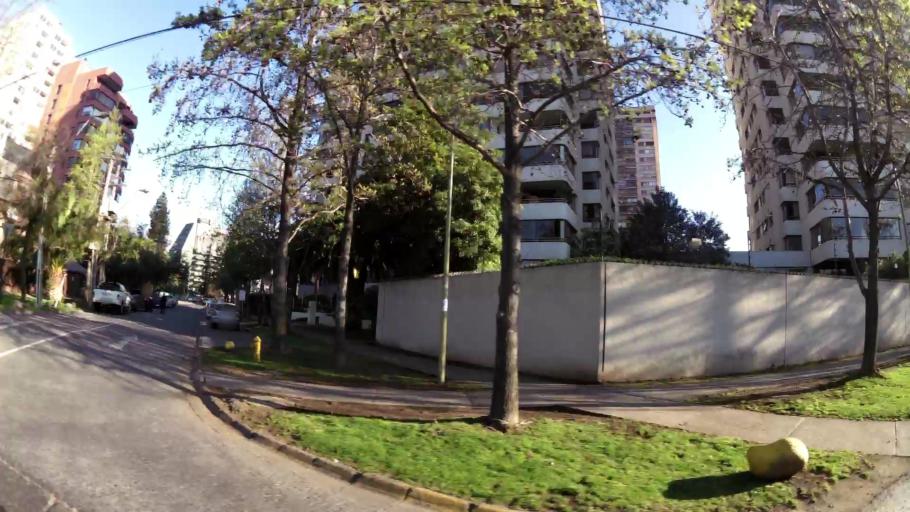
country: CL
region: Santiago Metropolitan
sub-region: Provincia de Santiago
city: Villa Presidente Frei, Nunoa, Santiago, Chile
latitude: -33.4063
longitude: -70.5848
